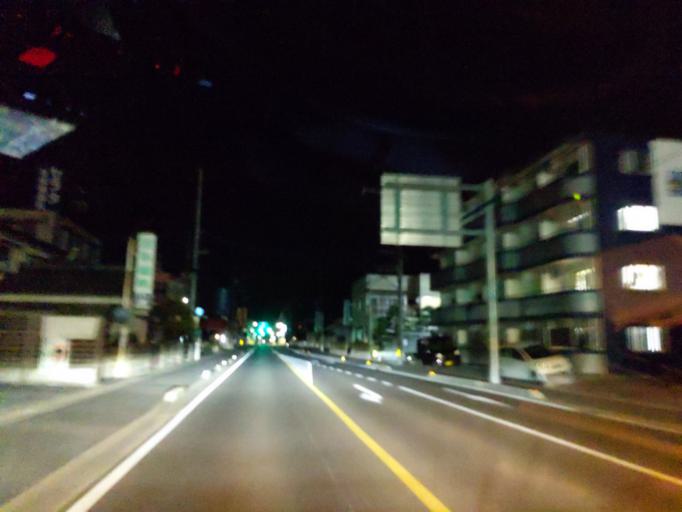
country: JP
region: Okayama
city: Okayama-shi
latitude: 34.6893
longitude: 133.9586
